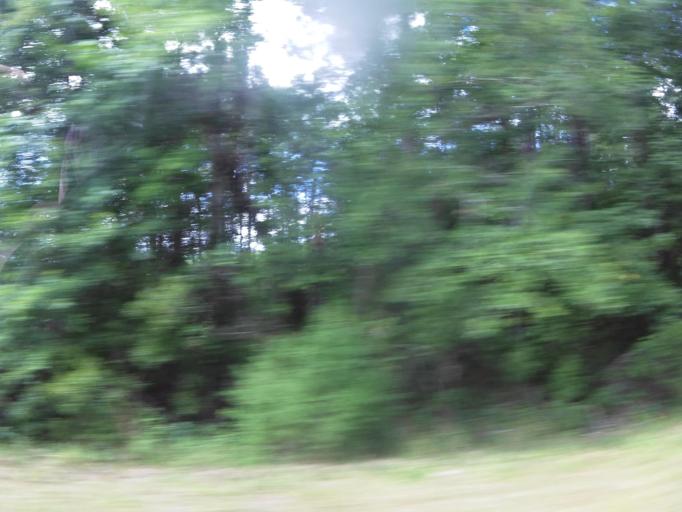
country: US
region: Florida
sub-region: Clay County
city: Asbury Lake
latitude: 29.9115
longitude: -81.8860
